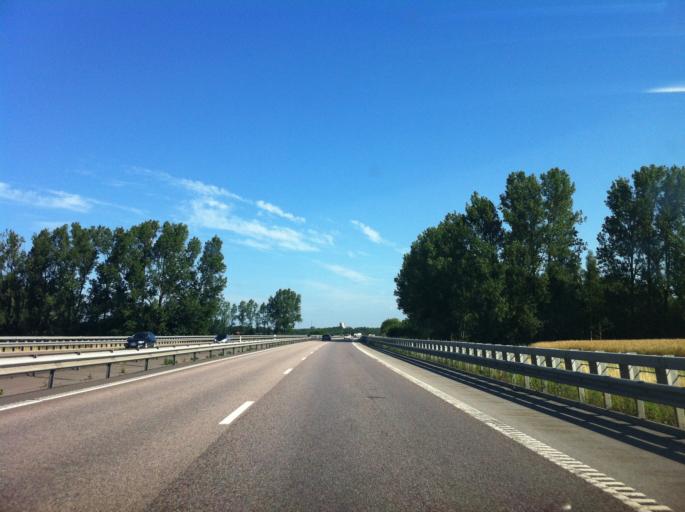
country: SE
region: Skane
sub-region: Helsingborg
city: Gantofta
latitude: 55.9839
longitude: 12.7828
